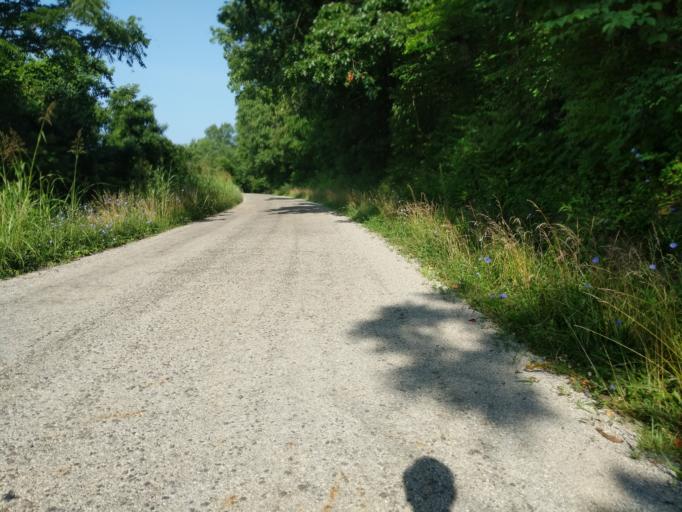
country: US
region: Ohio
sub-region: Athens County
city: Athens
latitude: 39.3452
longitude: -82.1100
